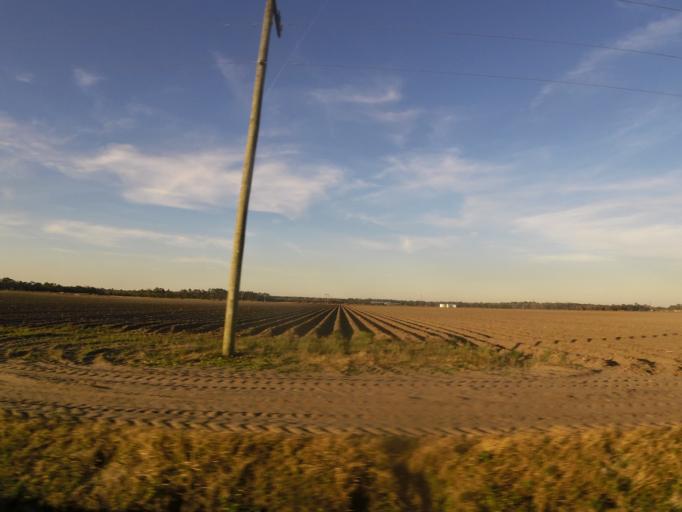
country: US
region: Florida
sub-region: Putnam County
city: East Palatka
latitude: 29.7908
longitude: -81.4945
